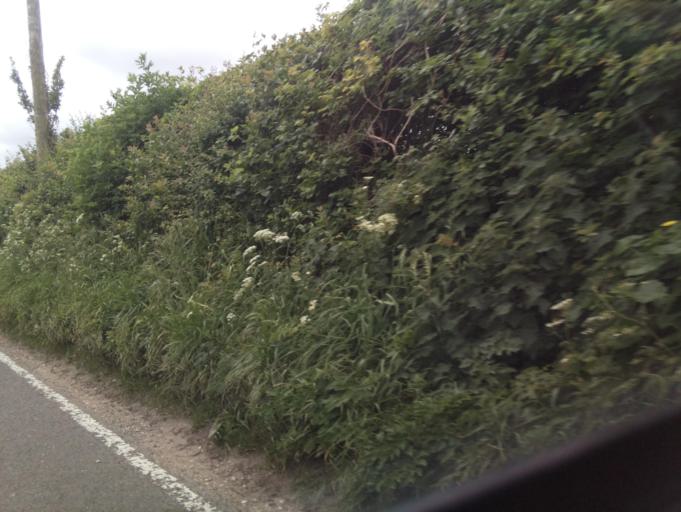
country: GB
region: England
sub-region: Dorset
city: Dorchester
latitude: 50.7453
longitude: -2.4612
